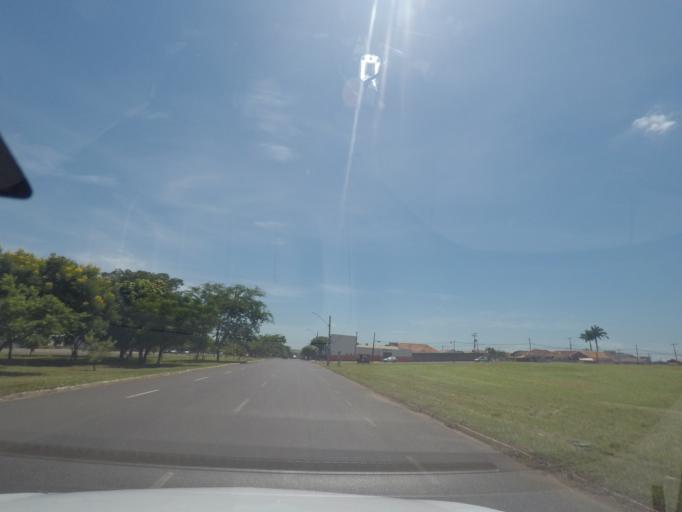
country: BR
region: Sao Paulo
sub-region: Matao
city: Matao
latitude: -21.6188
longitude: -48.3558
